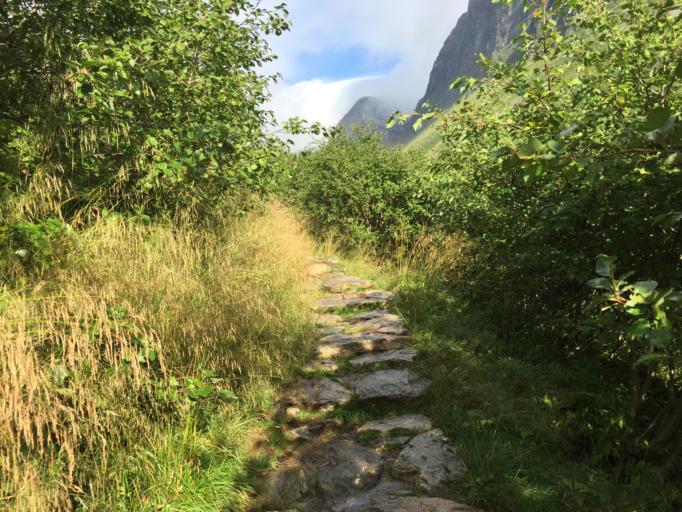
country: NO
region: More og Romsdal
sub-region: Norddal
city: Valldal
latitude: 62.1040
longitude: 7.2231
